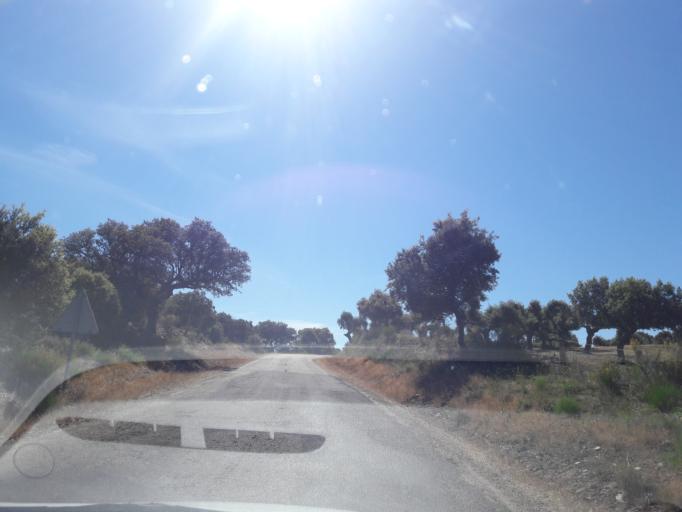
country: ES
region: Castille and Leon
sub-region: Provincia de Salamanca
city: Juzbado
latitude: 41.0642
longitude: -5.8985
